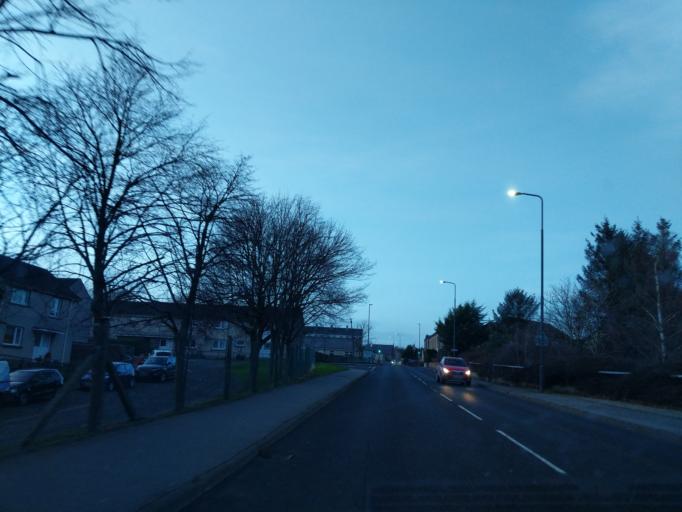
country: GB
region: Scotland
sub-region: Midlothian
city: Bonnyrigg
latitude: 55.8725
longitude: -3.0999
